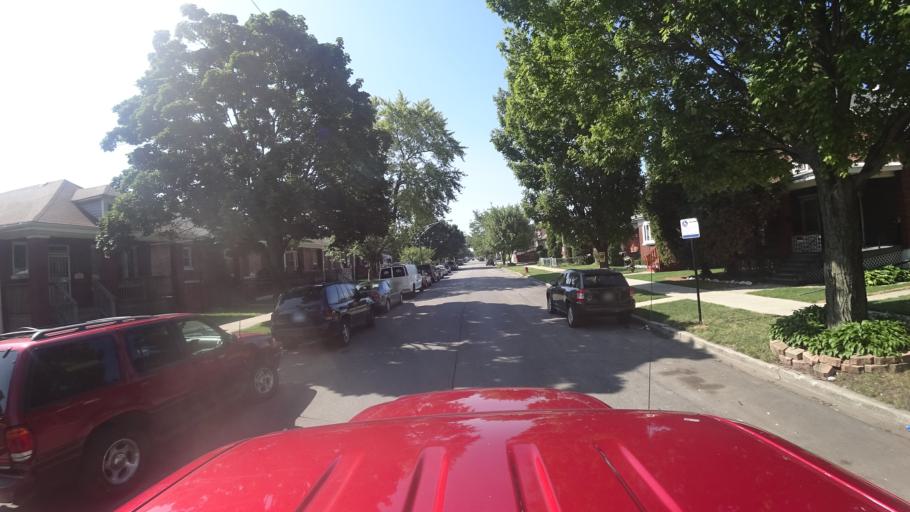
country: US
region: Illinois
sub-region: Cook County
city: Hometown
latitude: 41.7879
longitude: -87.6888
